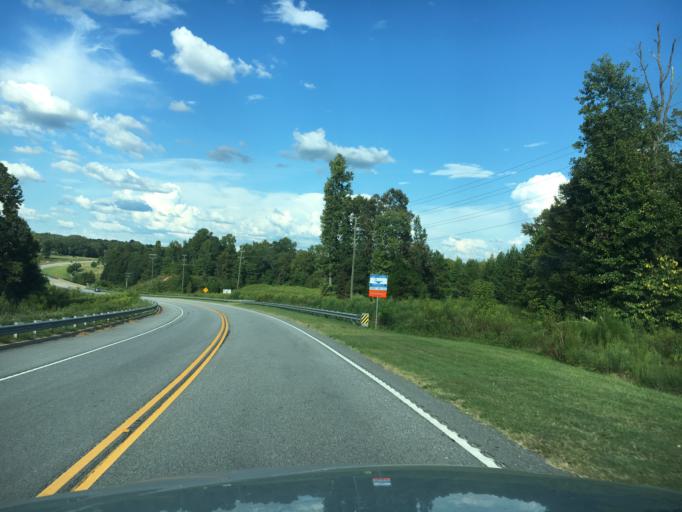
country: US
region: South Carolina
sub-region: Laurens County
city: Laurens
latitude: 34.5222
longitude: -82.1411
